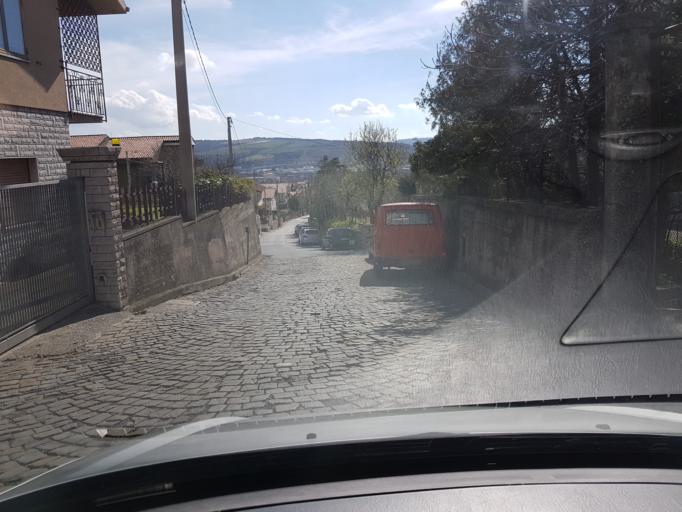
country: IT
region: Friuli Venezia Giulia
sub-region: Provincia di Trieste
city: Domio
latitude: 45.6218
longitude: 13.8365
